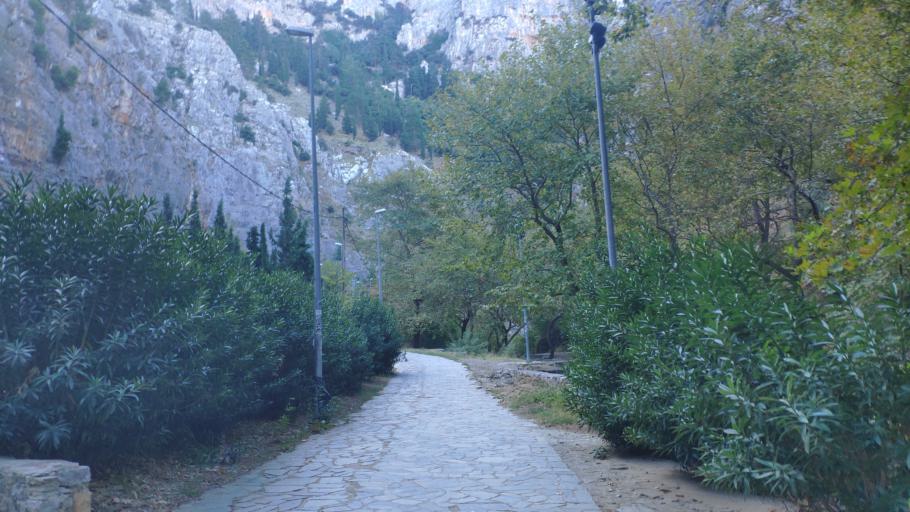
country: GR
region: Central Greece
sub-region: Nomos Voiotias
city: Livadeia
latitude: 38.4310
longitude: 22.8751
